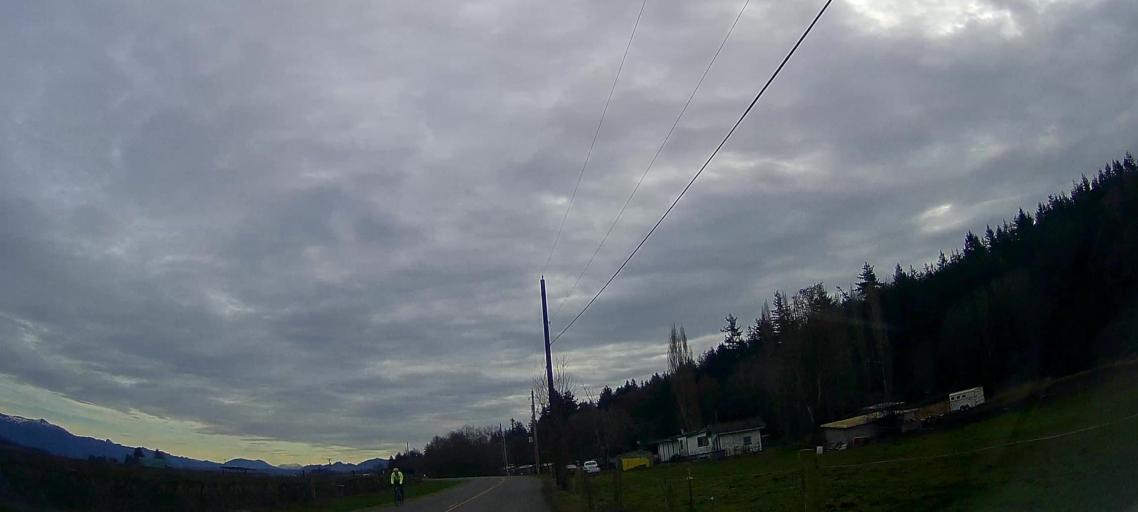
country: US
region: Washington
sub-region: Skagit County
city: Burlington
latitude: 48.5046
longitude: -122.4221
